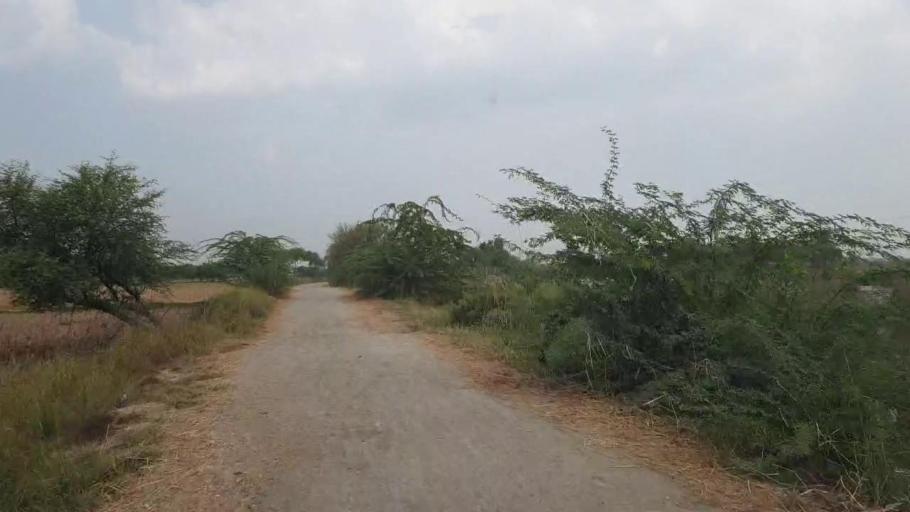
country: PK
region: Sindh
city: Matli
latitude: 24.9630
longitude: 68.7183
